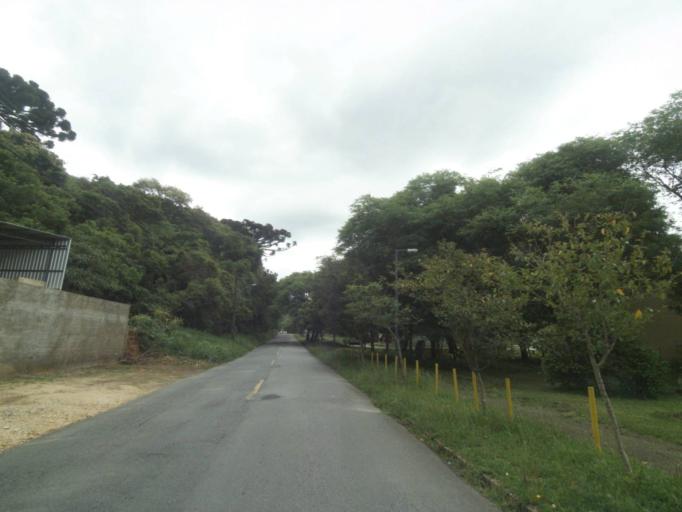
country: BR
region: Parana
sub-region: Curitiba
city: Curitiba
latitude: -25.3924
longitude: -49.2760
